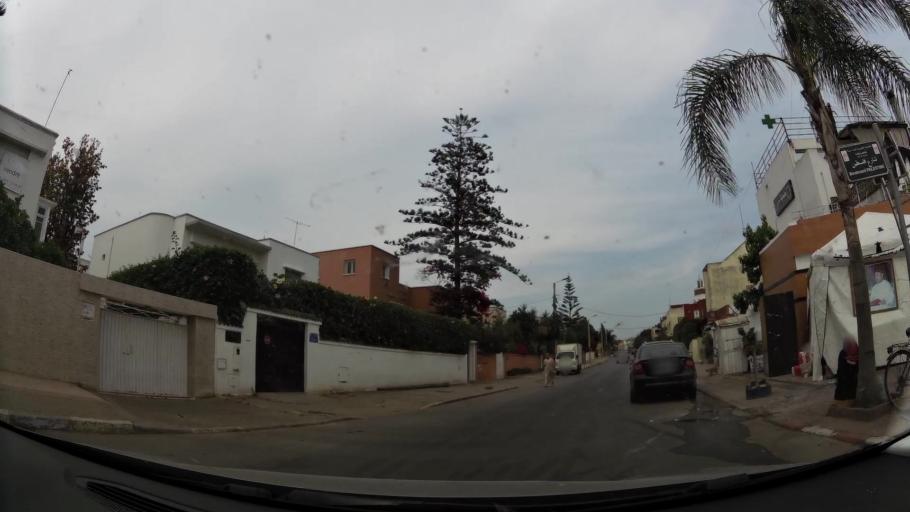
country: MA
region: Rabat-Sale-Zemmour-Zaer
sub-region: Rabat
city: Rabat
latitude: 34.0309
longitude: -6.8129
